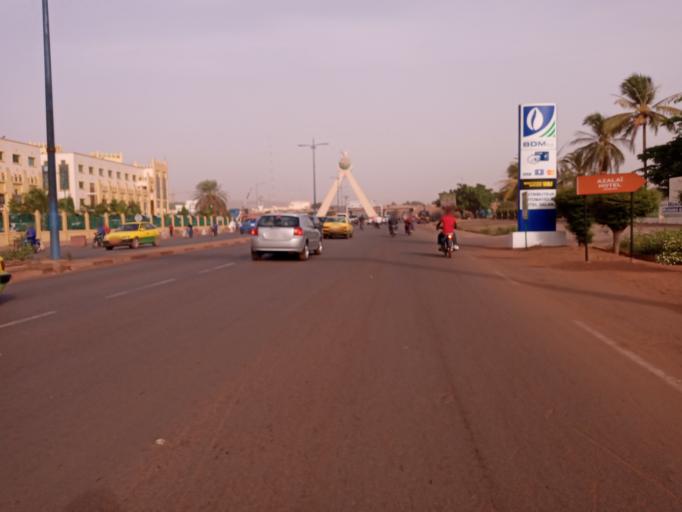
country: ML
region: Bamako
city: Bamako
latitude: 12.6302
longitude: -8.0095
